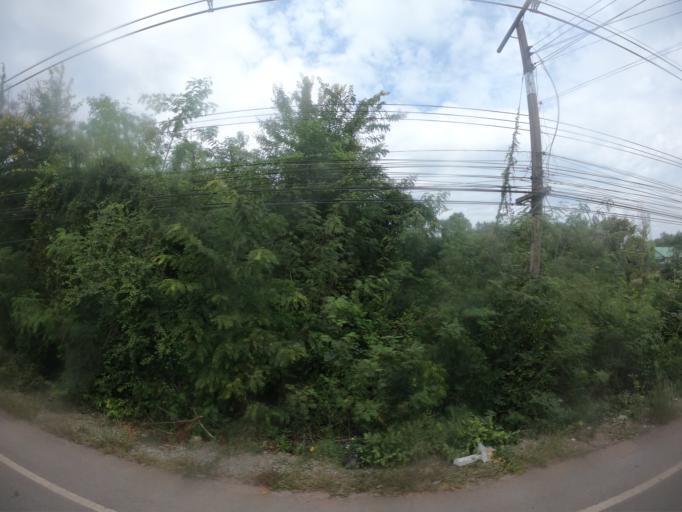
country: TH
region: Maha Sarakham
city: Kantharawichai
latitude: 16.3277
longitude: 103.2872
